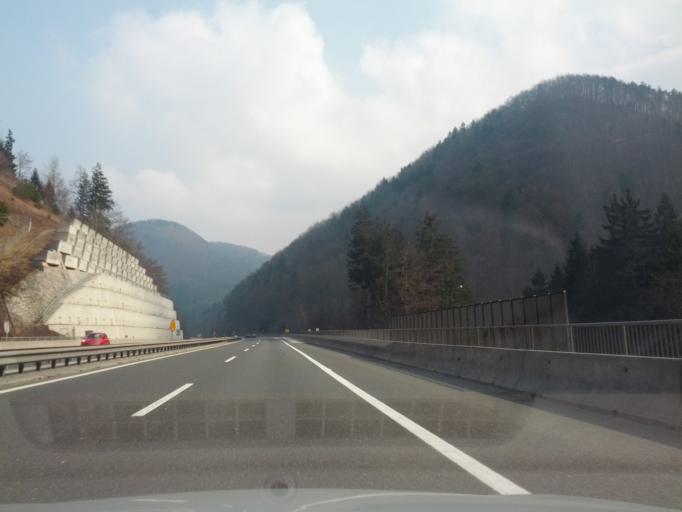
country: SI
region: Vransko
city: Vransko
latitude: 46.2177
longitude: 14.9259
